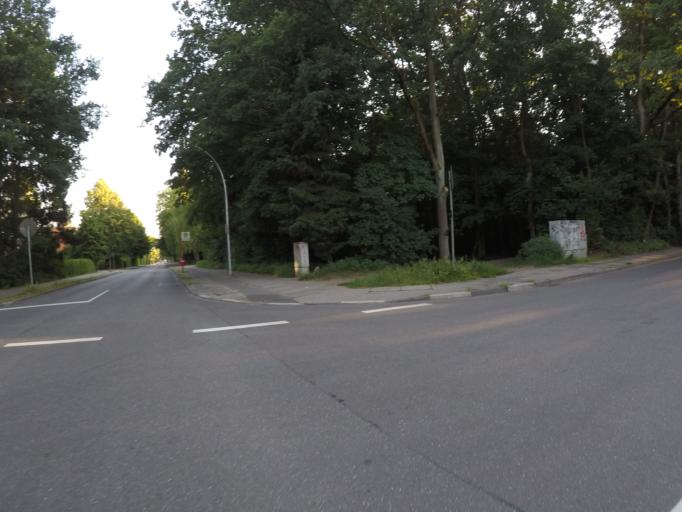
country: DE
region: Hamburg
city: Poppenbuettel
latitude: 53.6592
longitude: 10.0955
